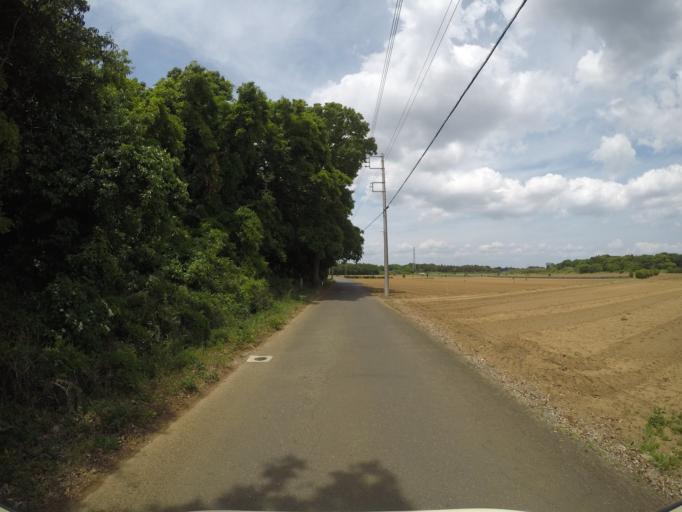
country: JP
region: Ibaraki
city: Ushiku
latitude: 35.9782
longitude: 140.1167
